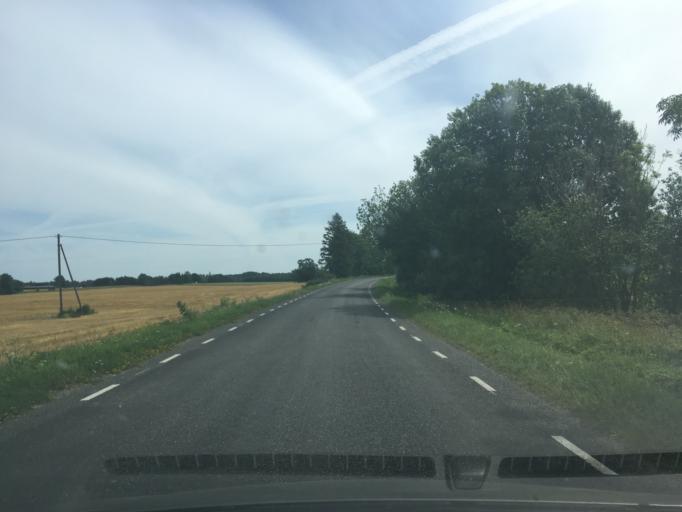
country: EE
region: Raplamaa
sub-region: Kohila vald
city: Kohila
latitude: 59.1188
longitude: 24.8440
